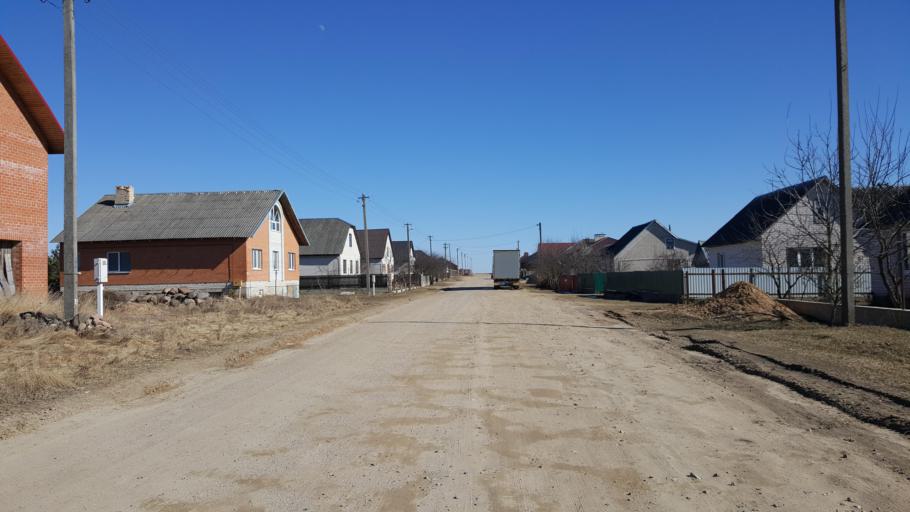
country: BY
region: Brest
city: Kamyanyets
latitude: 52.4042
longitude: 23.8437
